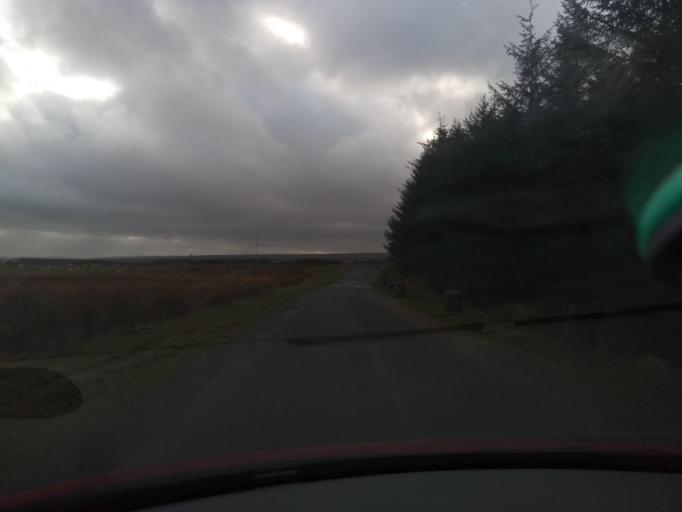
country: GB
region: England
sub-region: Northumberland
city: Rochester
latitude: 55.2866
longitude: -2.2800
